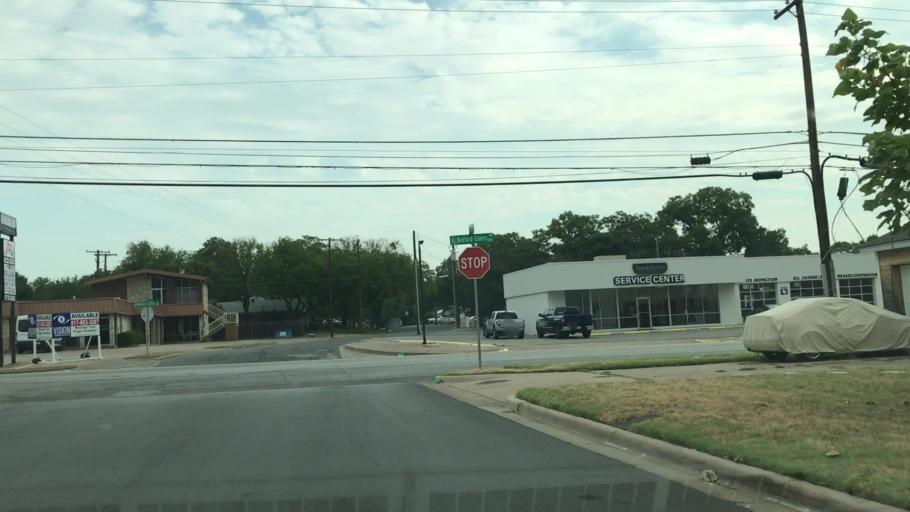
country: US
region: Texas
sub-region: Tarrant County
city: Hurst
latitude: 32.8336
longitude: -97.1698
